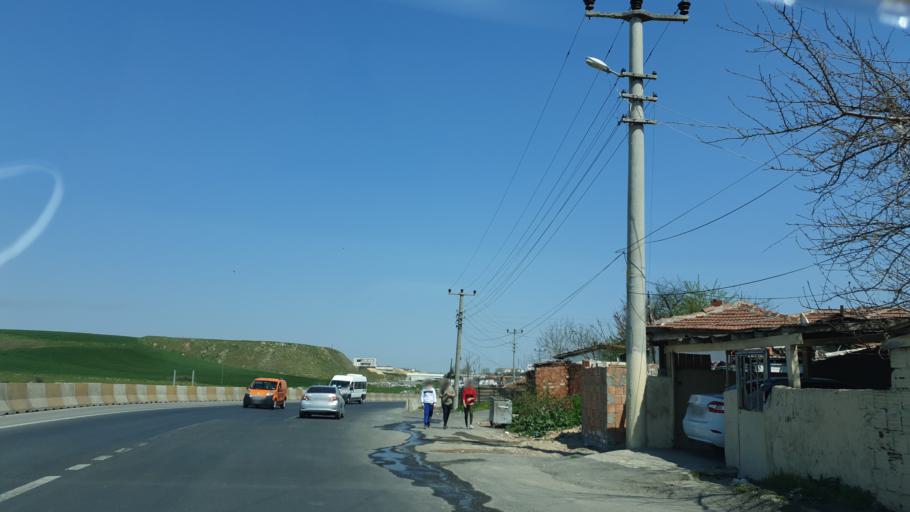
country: TR
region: Tekirdag
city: Corlu
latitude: 41.1687
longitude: 27.7952
